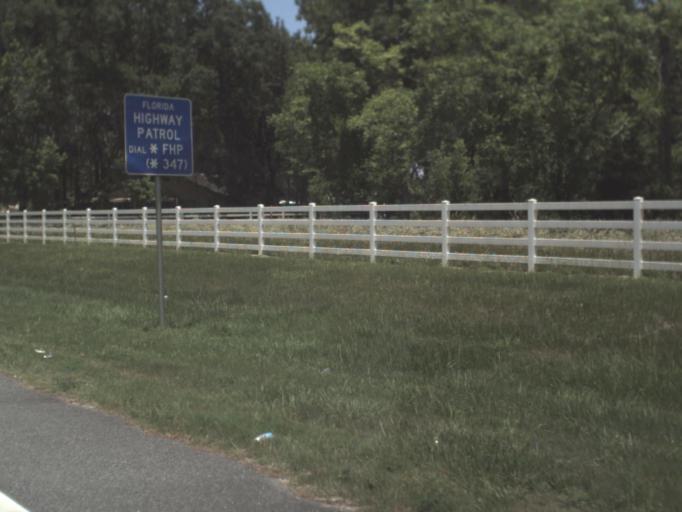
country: US
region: Florida
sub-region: Levy County
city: Manatee Road
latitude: 29.6090
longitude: -82.9827
